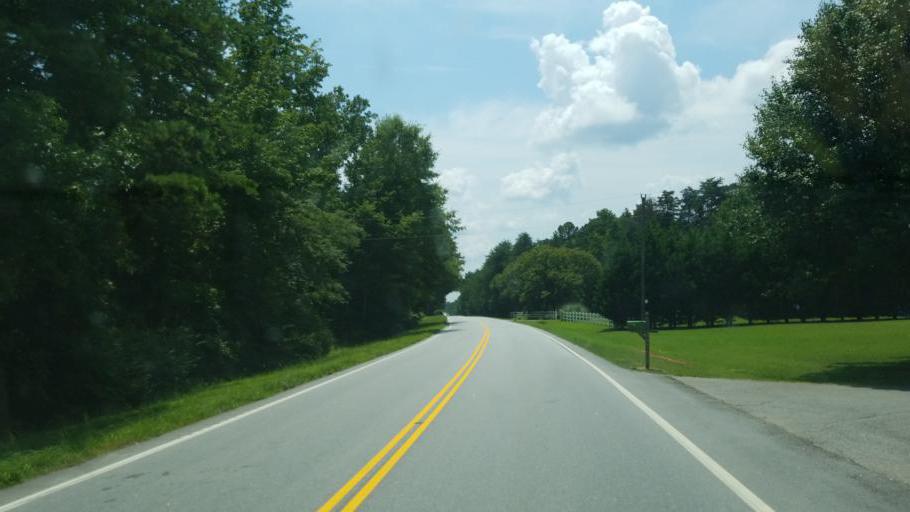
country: US
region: North Carolina
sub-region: Cleveland County
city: Kings Mountain
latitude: 35.1572
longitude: -81.3258
